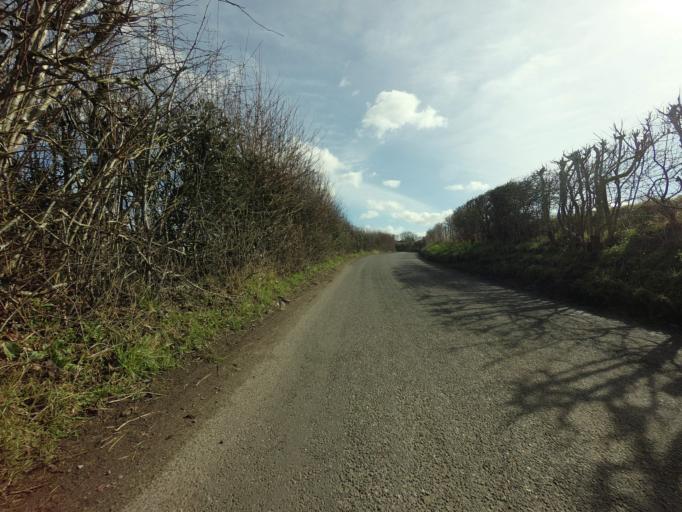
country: GB
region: England
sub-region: Kent
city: Shoreham
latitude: 51.3531
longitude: 0.1592
